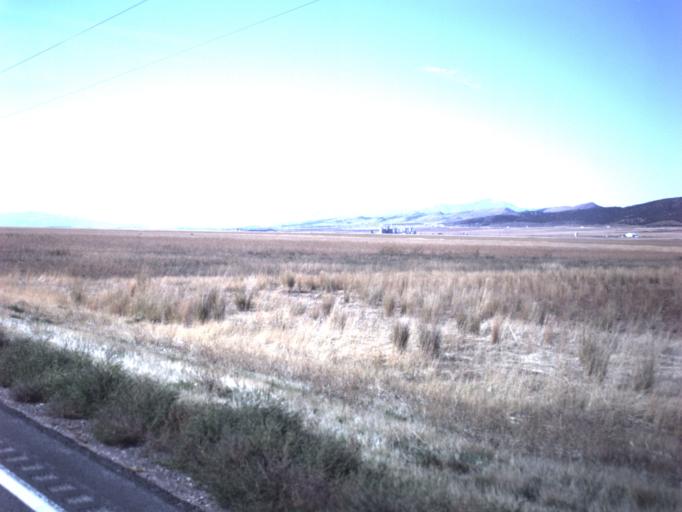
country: US
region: Utah
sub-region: Juab County
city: Nephi
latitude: 39.6389
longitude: -111.8615
